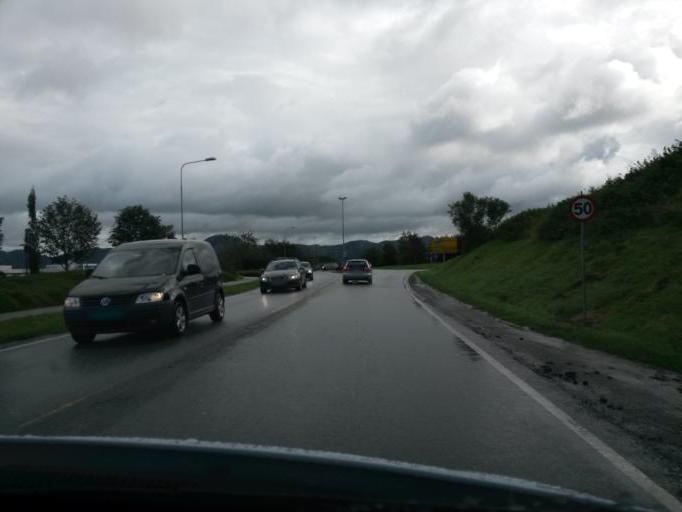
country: NO
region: Rogaland
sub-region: Sandnes
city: Sandnes
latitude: 58.8865
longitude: 5.7143
